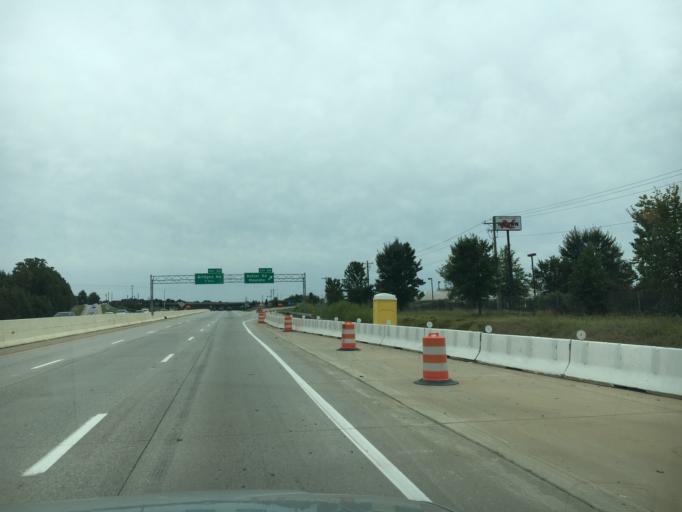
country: US
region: South Carolina
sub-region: Greenville County
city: Mauldin
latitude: 34.8097
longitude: -82.2859
